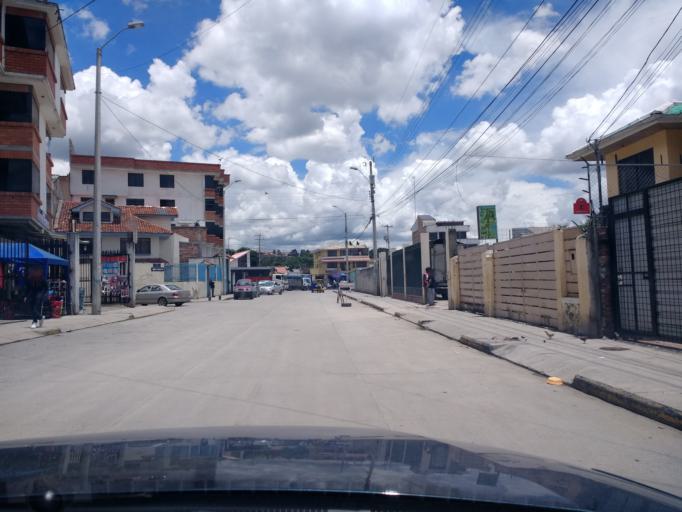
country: EC
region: Azuay
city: Cuenca
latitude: -2.8973
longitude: -79.0309
